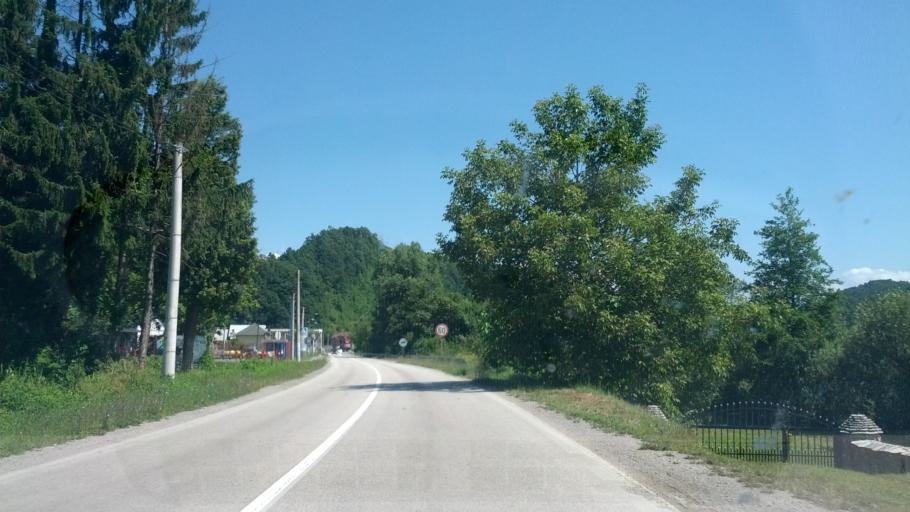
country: BA
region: Federation of Bosnia and Herzegovina
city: Otoka
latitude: 44.9365
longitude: 16.1604
